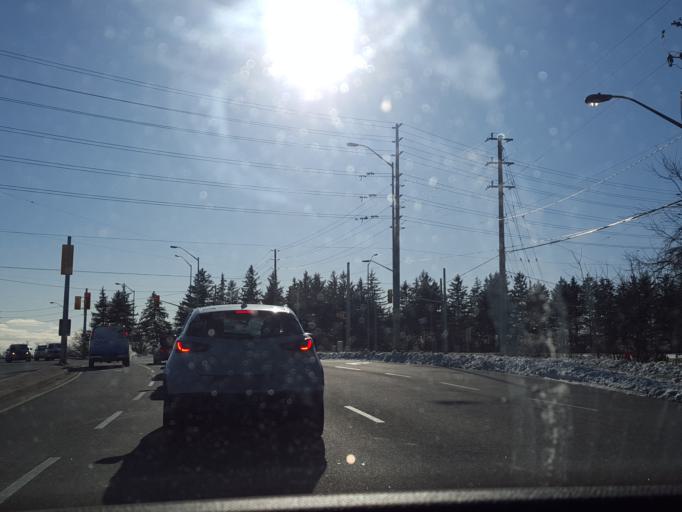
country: CA
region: Ontario
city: Oshawa
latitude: 43.9540
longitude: -78.9622
